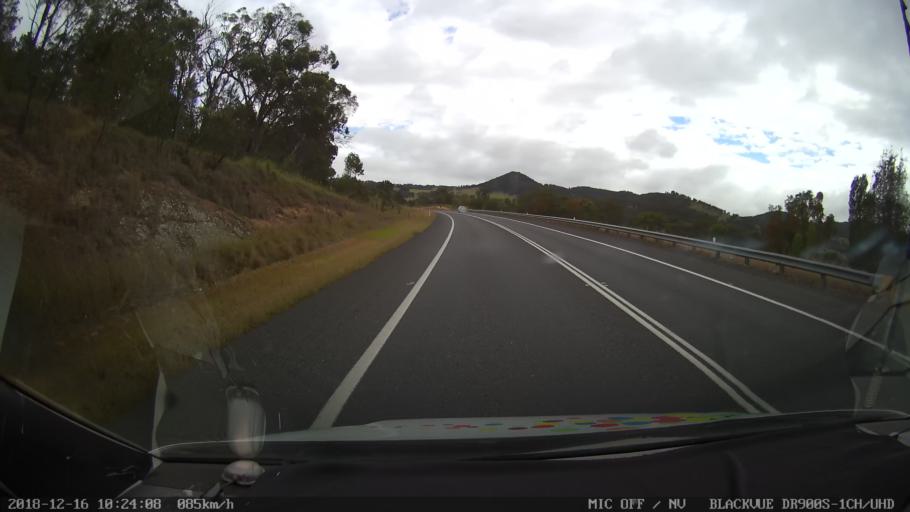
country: AU
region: New South Wales
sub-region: Tenterfield Municipality
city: Carrolls Creek
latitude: -29.1742
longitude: 152.0068
